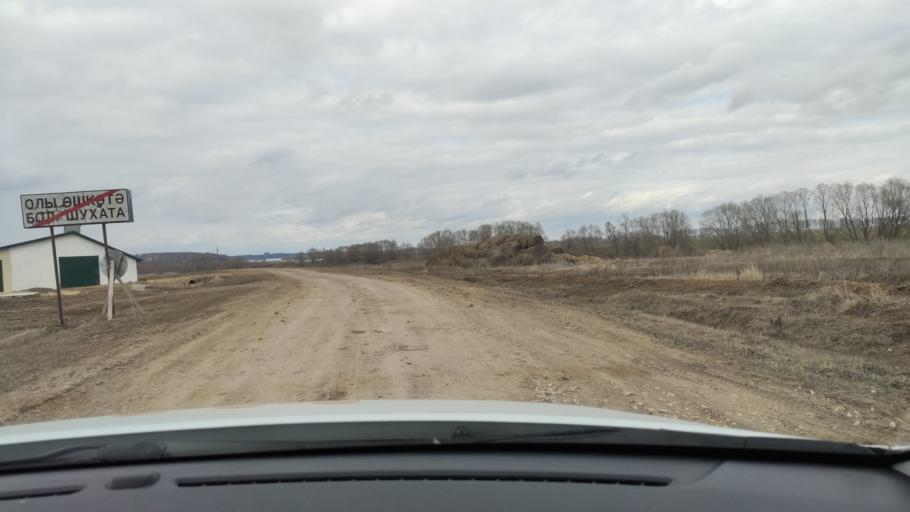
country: RU
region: Tatarstan
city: Vysokaya Gora
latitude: 56.2168
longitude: 49.3130
